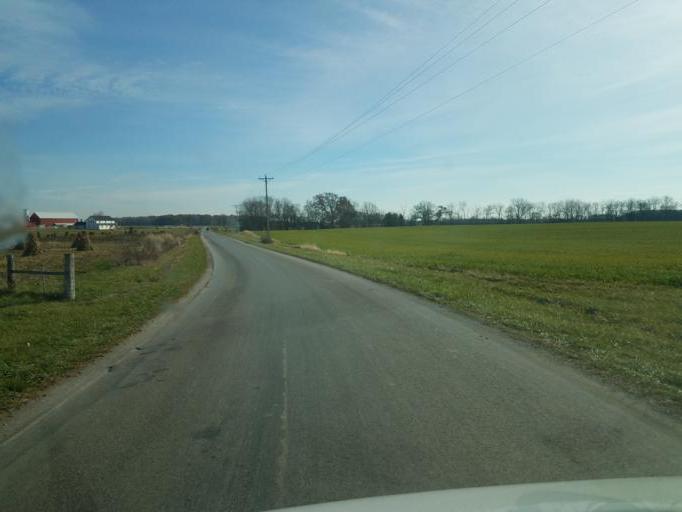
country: US
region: Ohio
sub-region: Hardin County
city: Kenton
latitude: 40.5673
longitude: -83.4507
